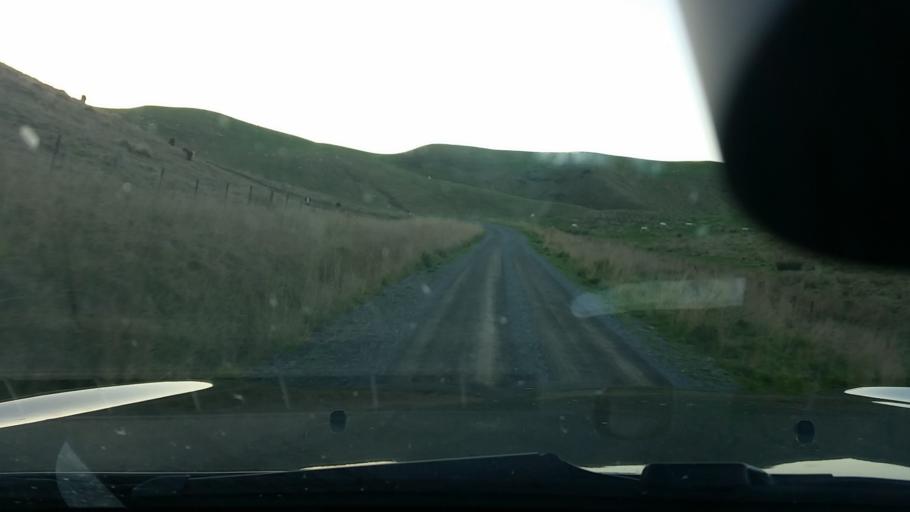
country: NZ
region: Marlborough
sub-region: Marlborough District
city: Blenheim
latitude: -41.7480
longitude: 174.0647
